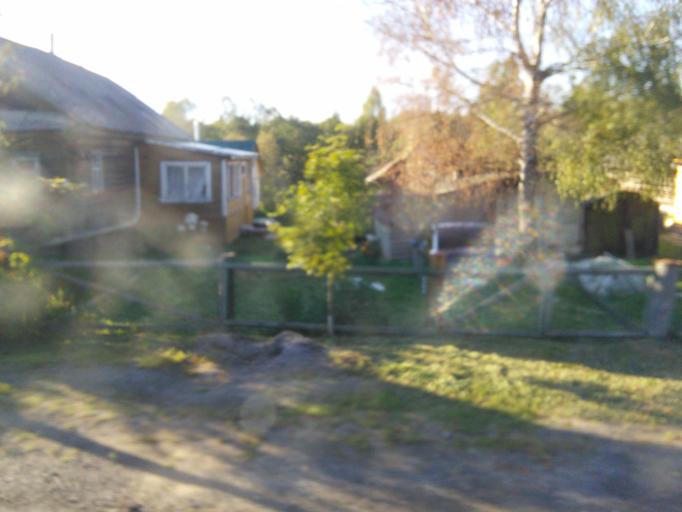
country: RU
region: Jaroslavl
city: Poshekhon'ye
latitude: 58.4555
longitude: 39.0372
